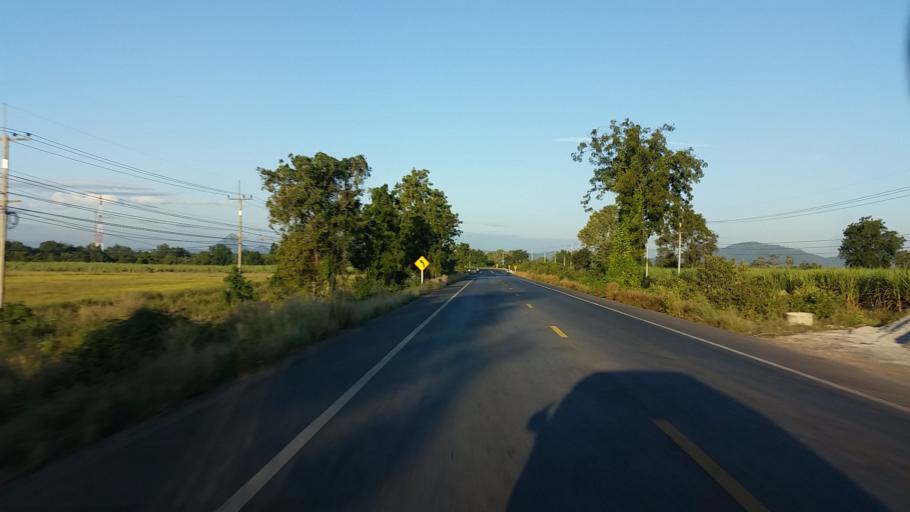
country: TH
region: Lop Buri
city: Chai Badan
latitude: 15.2653
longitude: 101.2011
